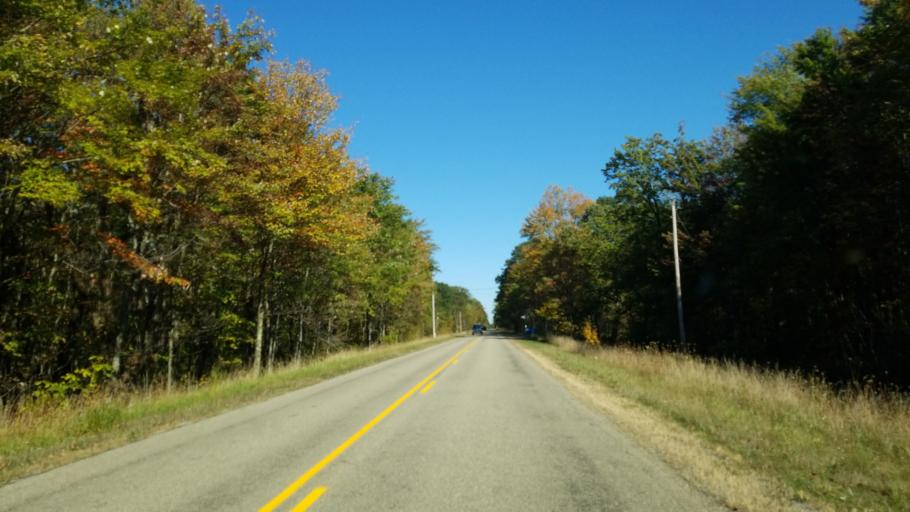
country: US
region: Pennsylvania
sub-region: Clearfield County
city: Shiloh
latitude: 41.2568
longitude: -78.3203
